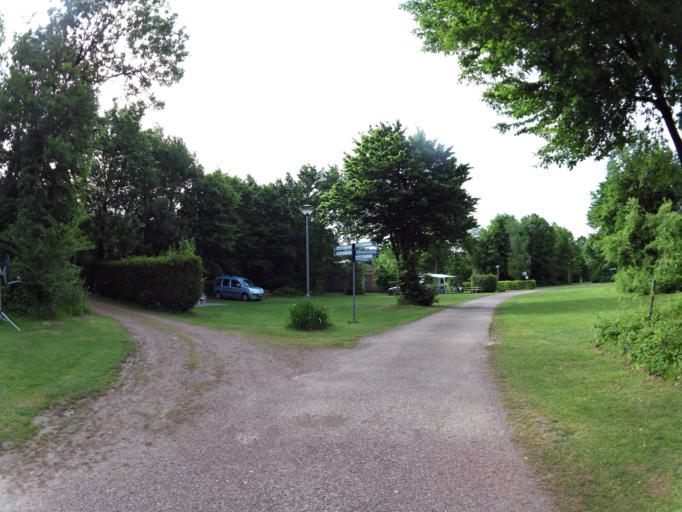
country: NL
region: Limburg
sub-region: Gemeente Kerkrade
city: Kerkrade
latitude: 50.9109
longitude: 6.0746
